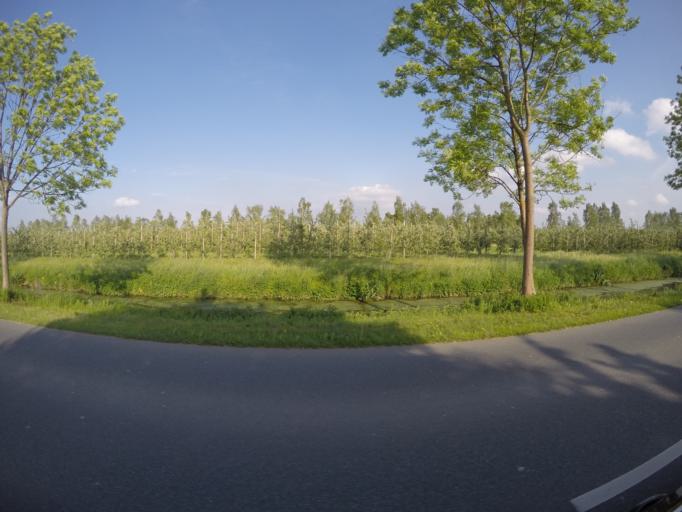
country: DE
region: Lower Saxony
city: Buxtehude
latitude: 53.4878
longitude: 9.6470
